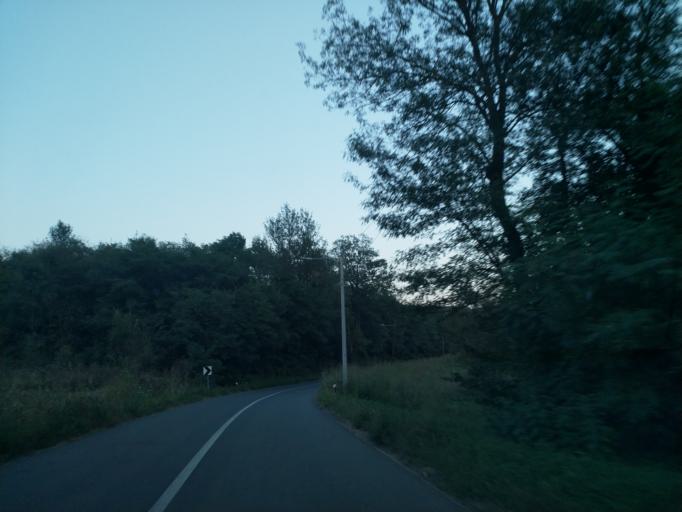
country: RS
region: Central Serbia
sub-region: Rasinski Okrug
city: Krusevac
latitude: 43.6273
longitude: 21.3338
